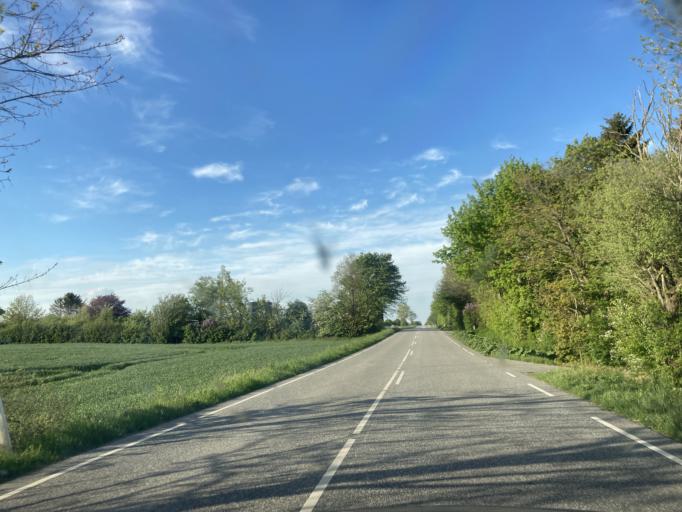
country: DK
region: South Denmark
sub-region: Faaborg-Midtfyn Kommune
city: Ringe
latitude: 55.1997
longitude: 10.5580
